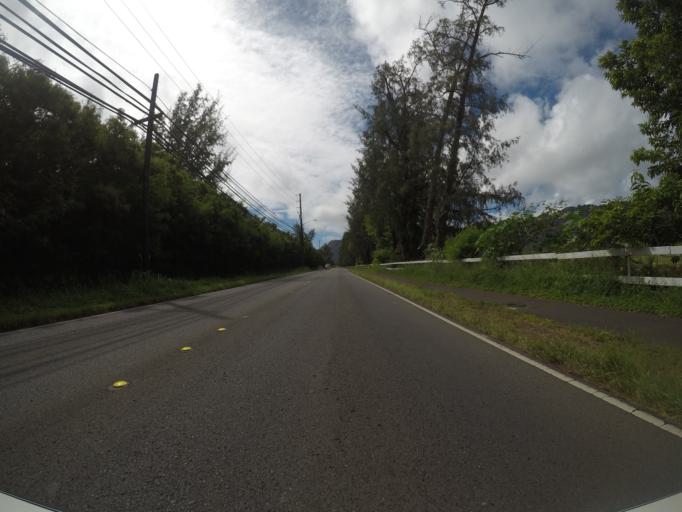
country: US
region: Hawaii
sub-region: Honolulu County
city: Waimanalo Beach
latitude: 21.3442
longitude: -157.7090
